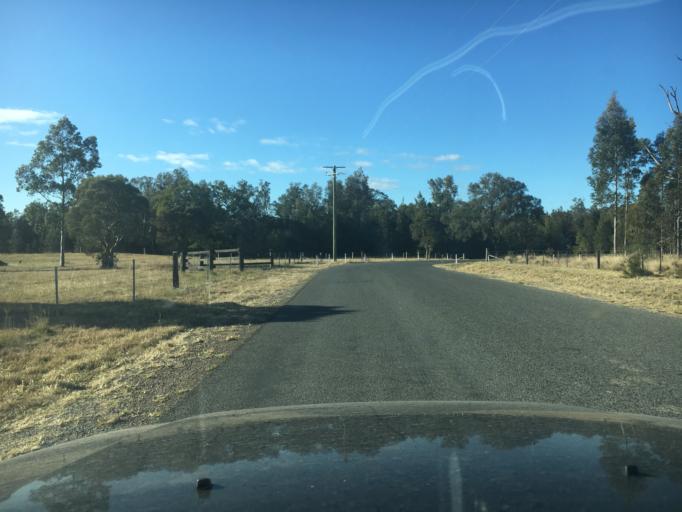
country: AU
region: New South Wales
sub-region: Singleton
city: Singleton
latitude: -32.5415
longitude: 151.2419
